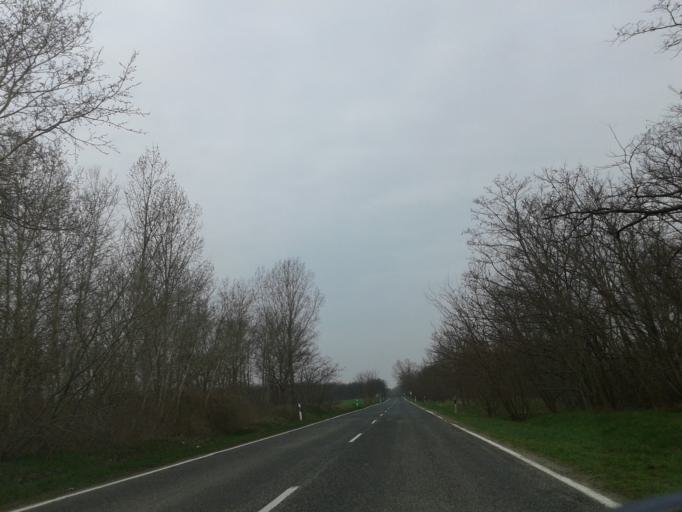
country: HU
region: Gyor-Moson-Sopron
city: Bony
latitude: 47.7317
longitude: 17.8619
